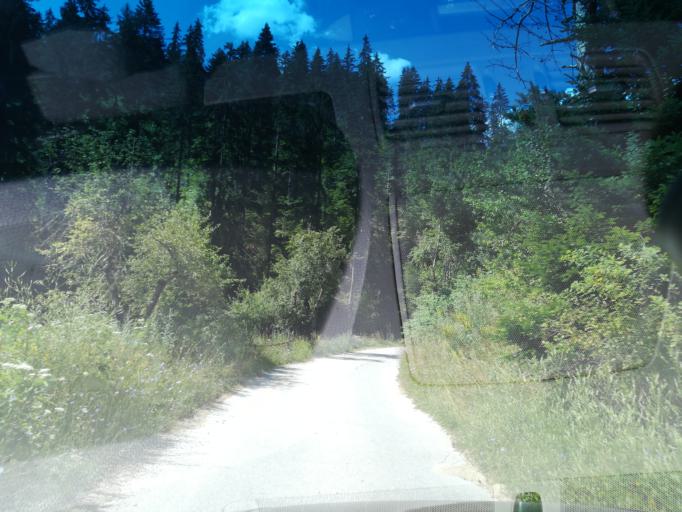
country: BG
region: Smolyan
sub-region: Obshtina Smolyan
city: Smolyan
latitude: 41.6602
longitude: 24.8133
